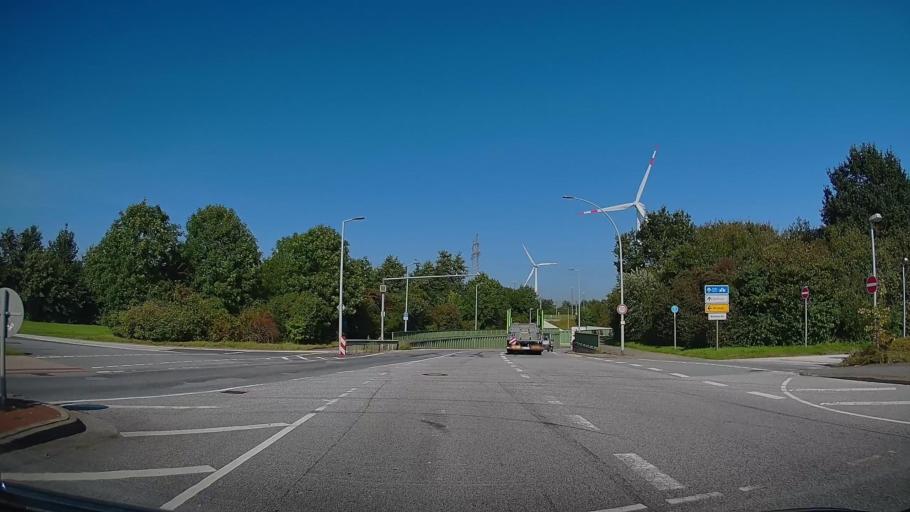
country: DE
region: Lower Saxony
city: Langen
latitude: 53.5963
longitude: 8.5398
